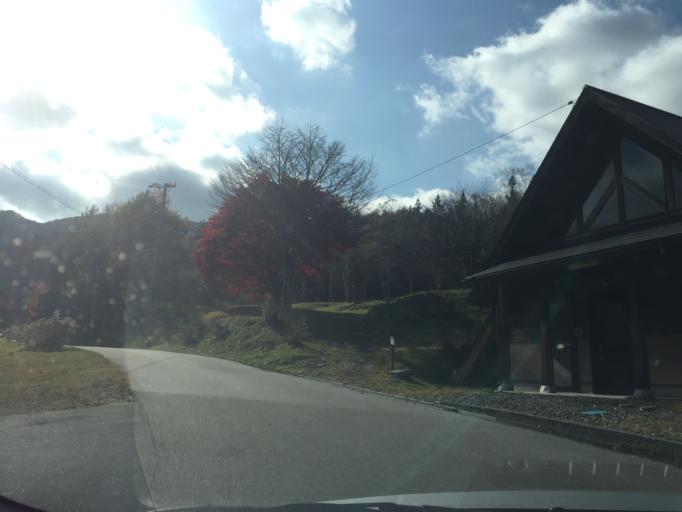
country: JP
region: Gifu
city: Nakatsugawa
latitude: 35.3692
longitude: 137.6698
